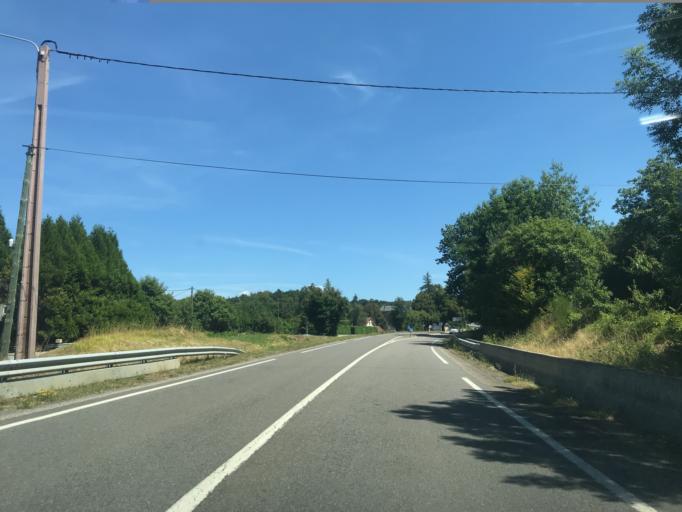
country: FR
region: Limousin
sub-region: Departement de la Correze
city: Naves
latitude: 45.3111
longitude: 1.8261
